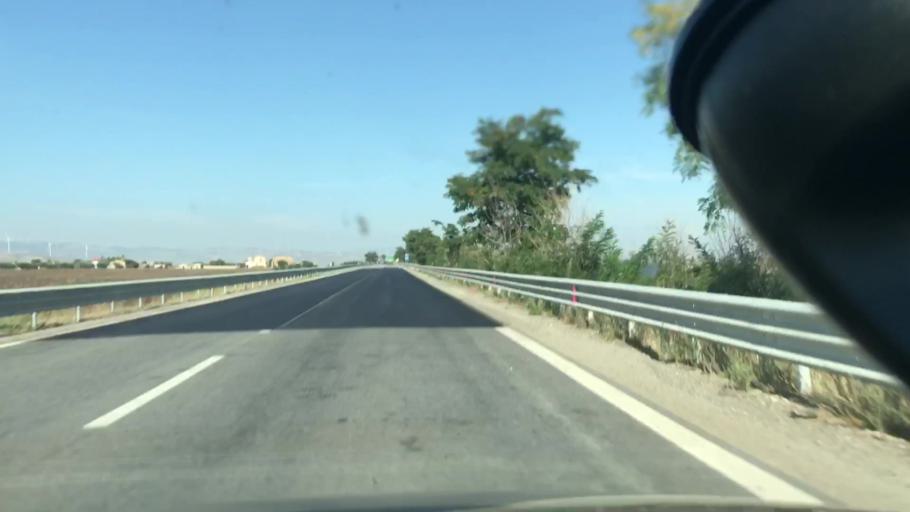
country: IT
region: Basilicate
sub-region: Provincia di Potenza
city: Zona 179
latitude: 41.0722
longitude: 15.6514
